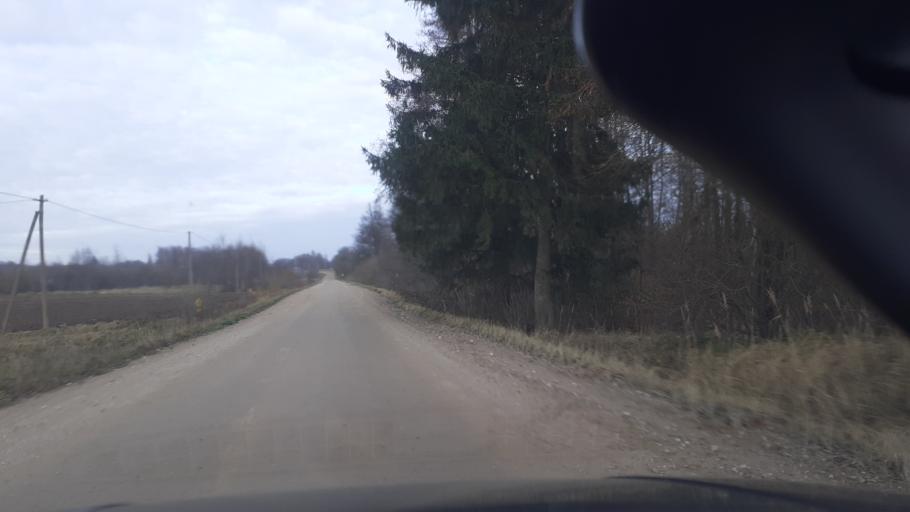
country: LV
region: Alsunga
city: Alsunga
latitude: 56.9091
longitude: 21.6560
